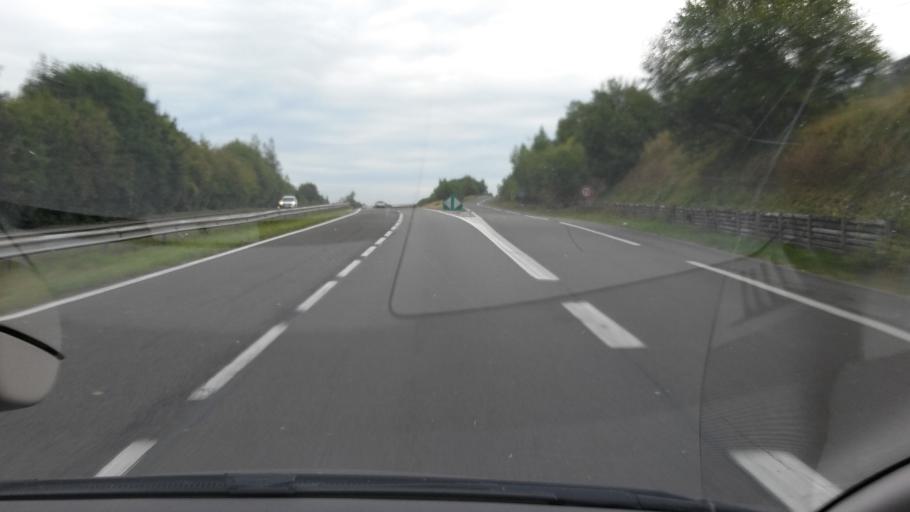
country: FR
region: Champagne-Ardenne
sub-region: Departement des Ardennes
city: La Francheville
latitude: 49.6759
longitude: 4.6576
